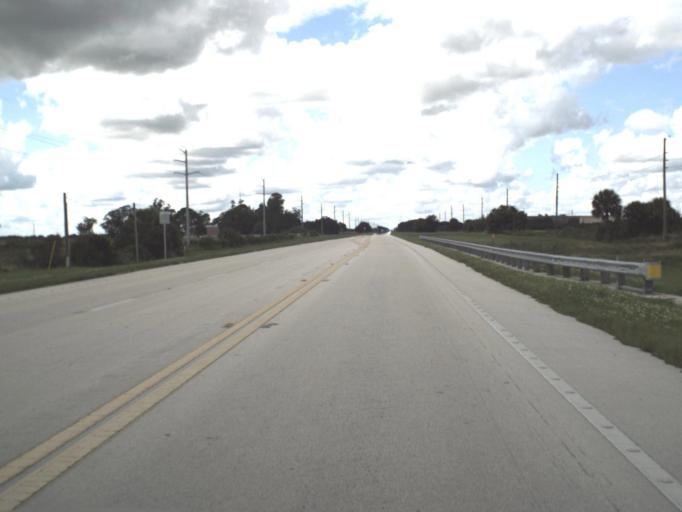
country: US
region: Florida
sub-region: Highlands County
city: Placid Lakes
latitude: 27.2097
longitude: -81.6135
